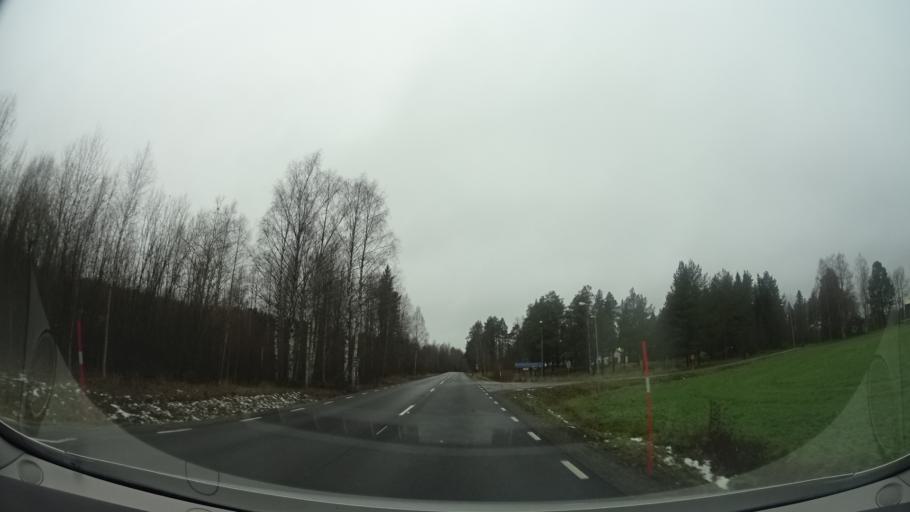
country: SE
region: Vaesterbotten
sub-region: Skelleftea Kommun
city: Kage
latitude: 64.8507
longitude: 20.8972
